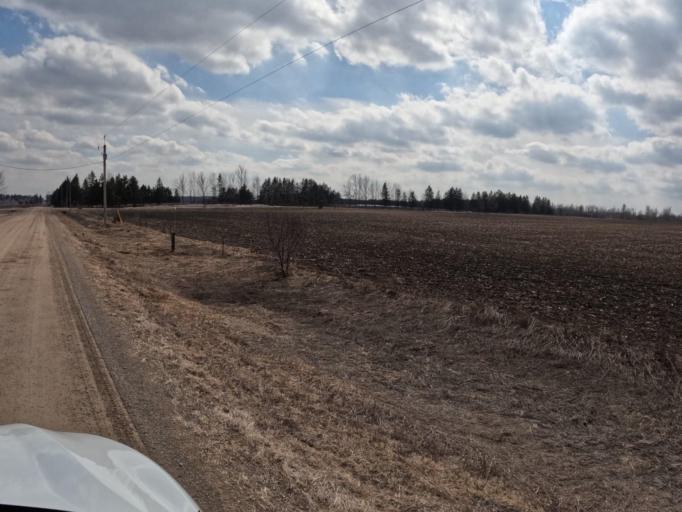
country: CA
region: Ontario
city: Shelburne
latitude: 43.9714
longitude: -80.2672
